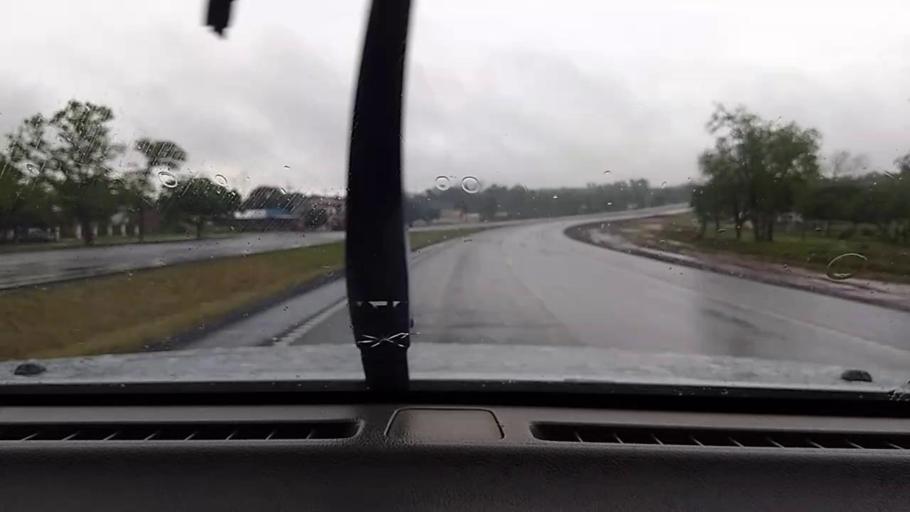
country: PY
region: Caaguazu
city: Repatriacion
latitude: -25.4658
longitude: -55.9336
